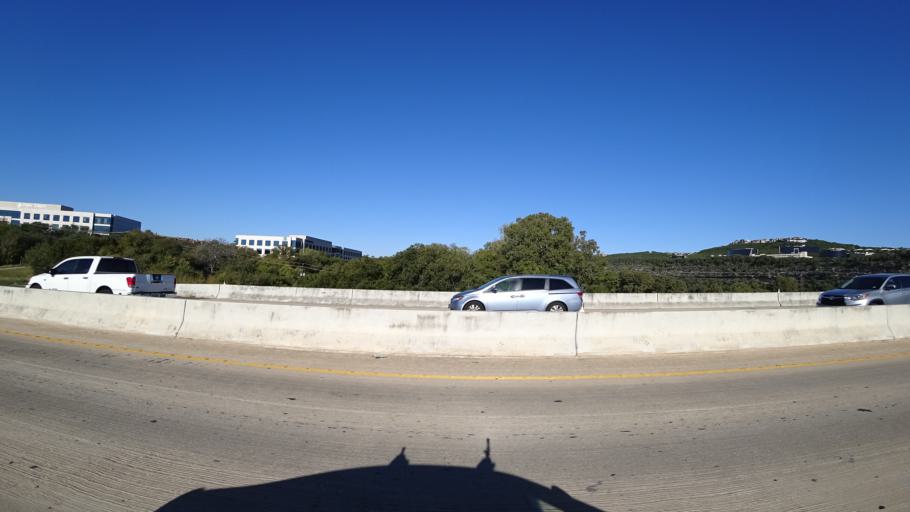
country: US
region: Texas
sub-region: Travis County
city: West Lake Hills
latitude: 30.3482
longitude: -97.7979
